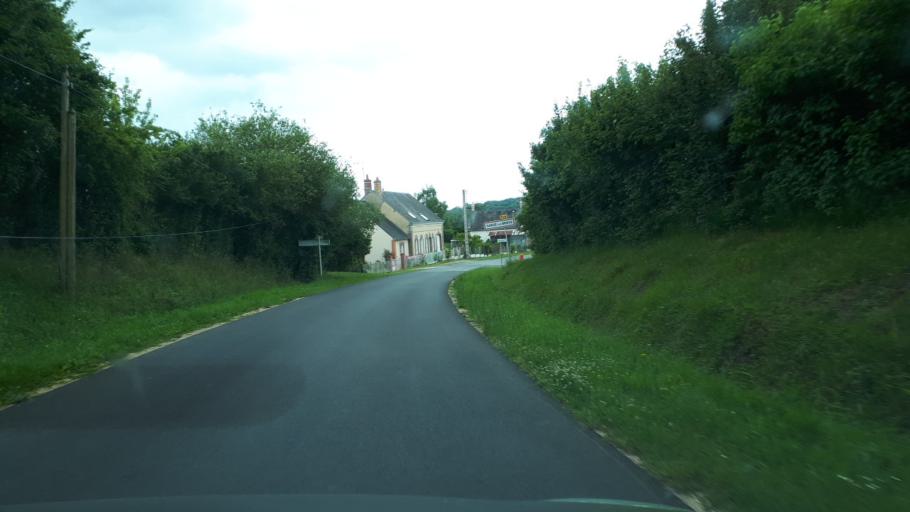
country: FR
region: Centre
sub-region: Departement du Loir-et-Cher
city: Sarge-sur-Braye
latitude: 47.9240
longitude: 0.8592
